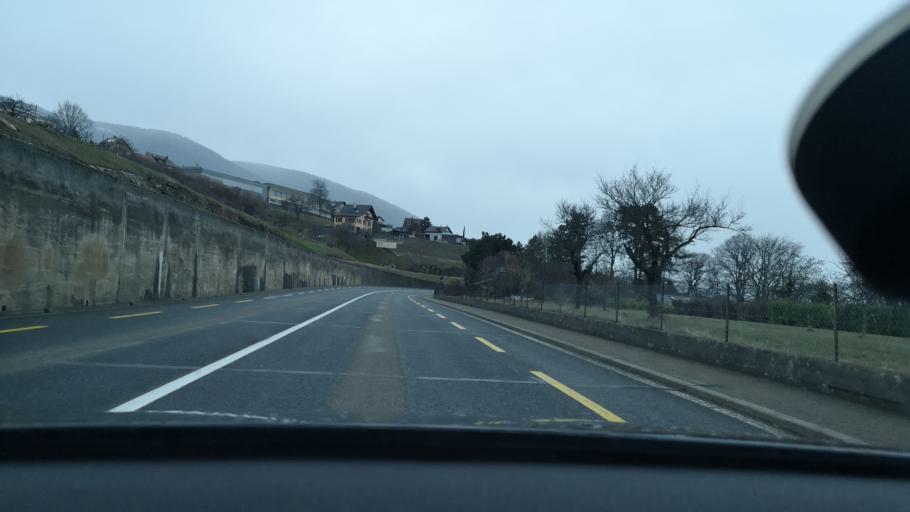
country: CH
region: Neuchatel
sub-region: Boudry District
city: Saint-Aubin-Sauges
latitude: 46.8836
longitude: 6.7630
